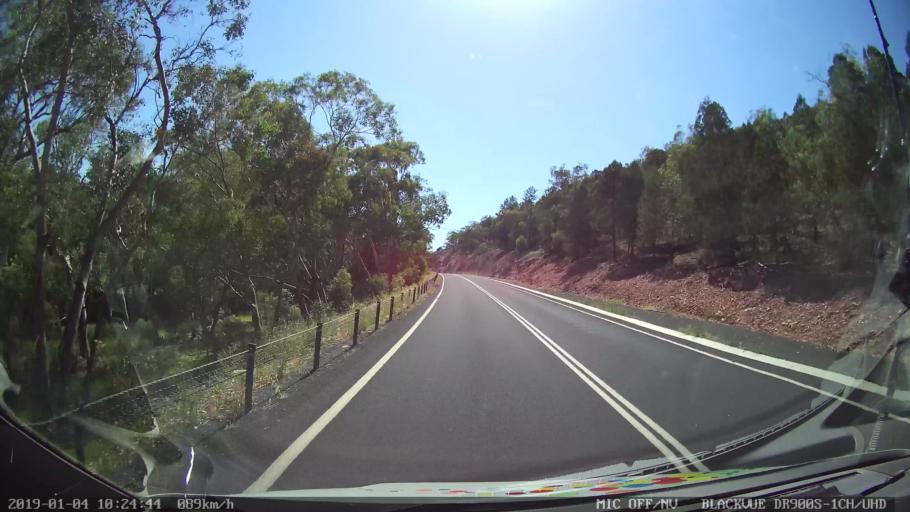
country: AU
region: New South Wales
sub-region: Cabonne
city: Canowindra
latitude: -33.3697
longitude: 148.5596
